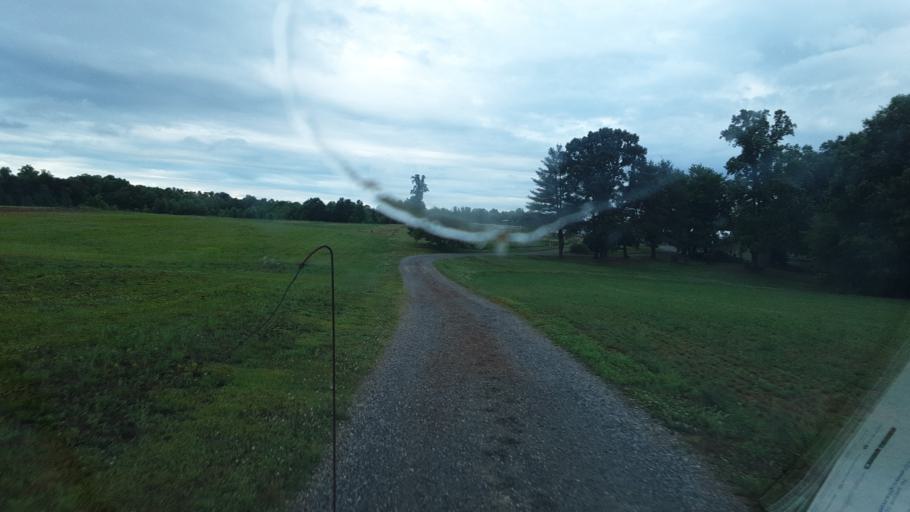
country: US
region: North Carolina
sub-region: Yadkin County
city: Yadkinville
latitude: 36.0523
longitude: -80.8251
